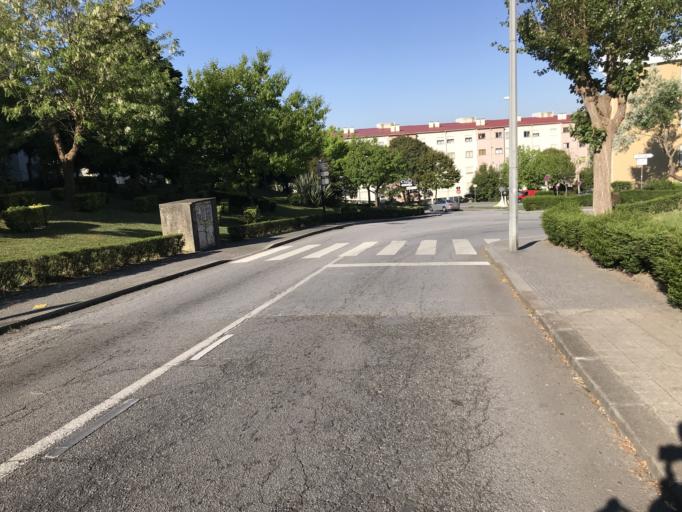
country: PT
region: Porto
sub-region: Matosinhos
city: Matosinhos
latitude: 41.1819
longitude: -8.6749
